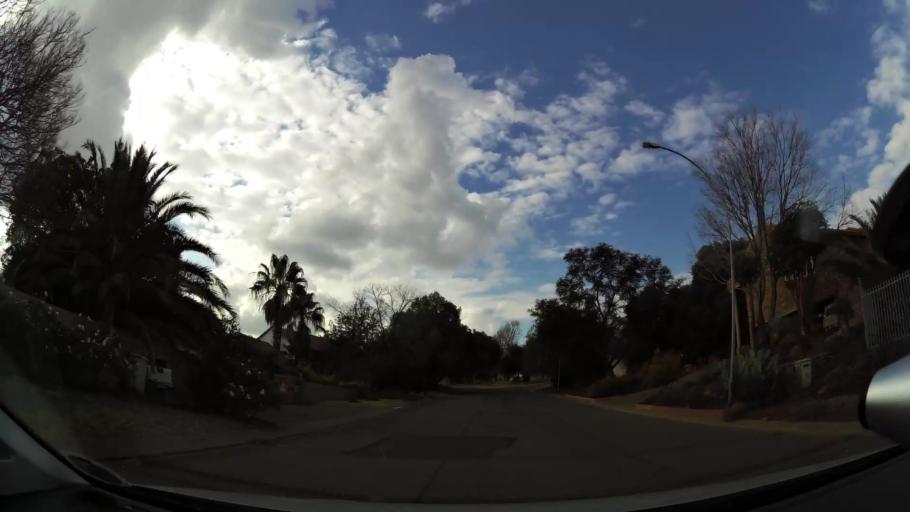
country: ZA
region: Orange Free State
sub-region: Mangaung Metropolitan Municipality
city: Bloemfontein
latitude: -29.0873
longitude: 26.1981
